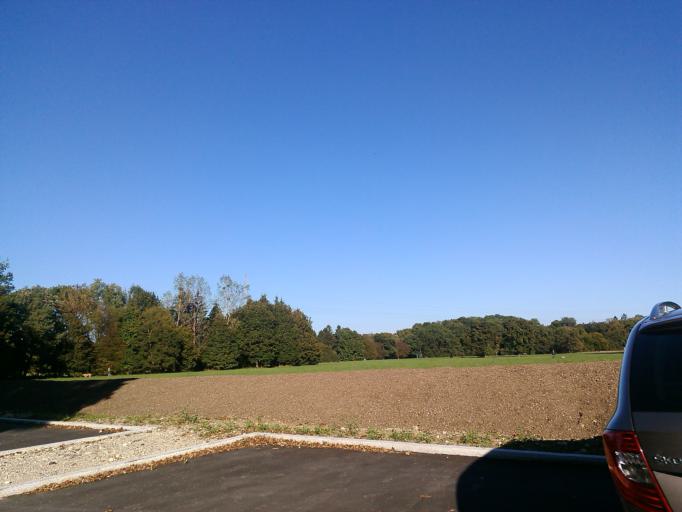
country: DE
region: Bavaria
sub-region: Upper Bavaria
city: Pasing
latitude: 48.1332
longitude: 11.4421
